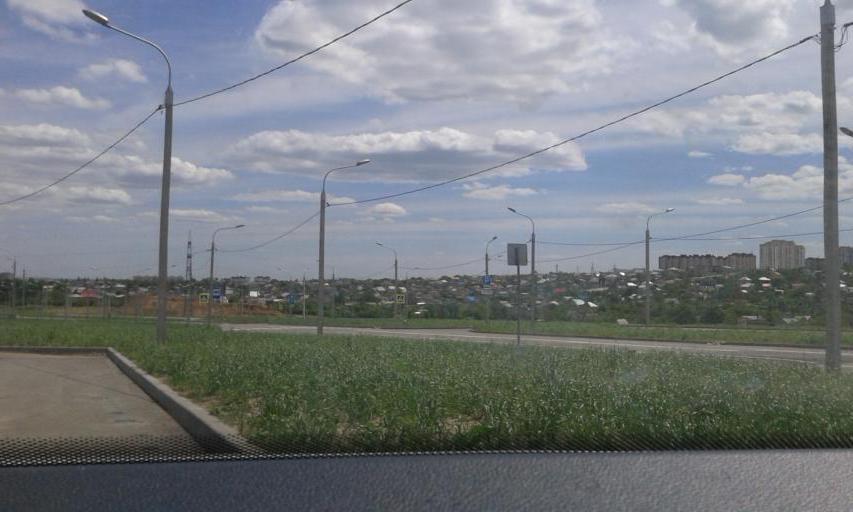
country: RU
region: Volgograd
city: Volgograd
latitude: 48.6593
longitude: 44.4063
